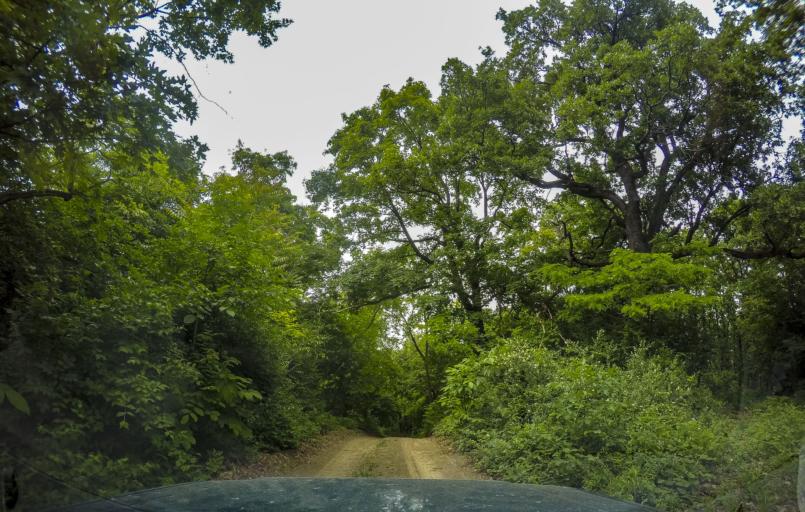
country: HU
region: Somogy
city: Balatonfoldvar
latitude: 46.7720
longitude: 17.8810
